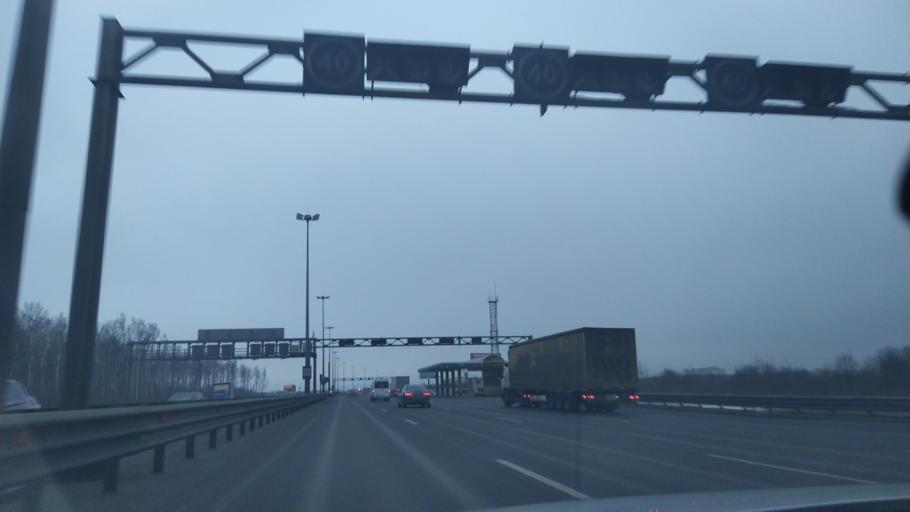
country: RU
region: Leningrad
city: Rybatskoye
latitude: 59.8779
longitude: 30.5295
